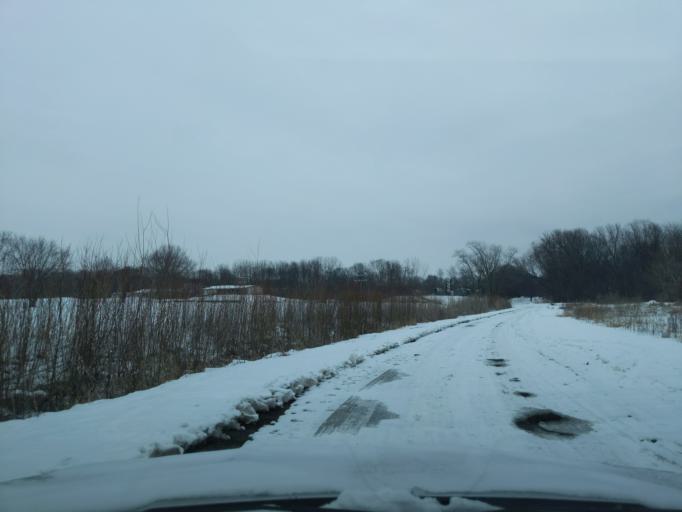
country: US
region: Indiana
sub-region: Tippecanoe County
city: West Lafayette
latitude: 40.4418
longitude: -86.8904
